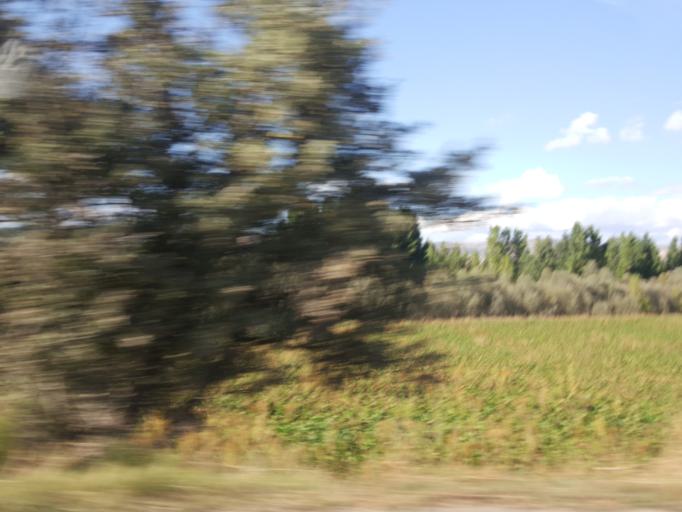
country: TR
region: Tokat
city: Yesilyurt
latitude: 40.0168
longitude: 36.2492
